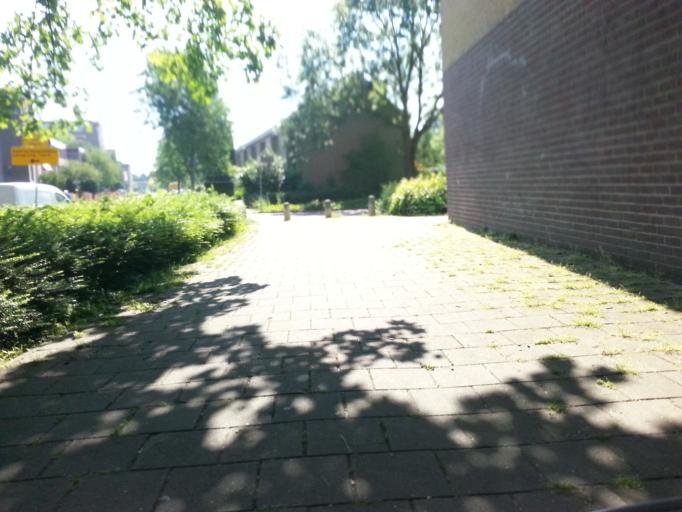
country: NL
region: Utrecht
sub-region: Gemeente Wijk bij Duurstede
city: Wijk bij Duurstede
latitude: 51.9727
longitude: 5.3368
